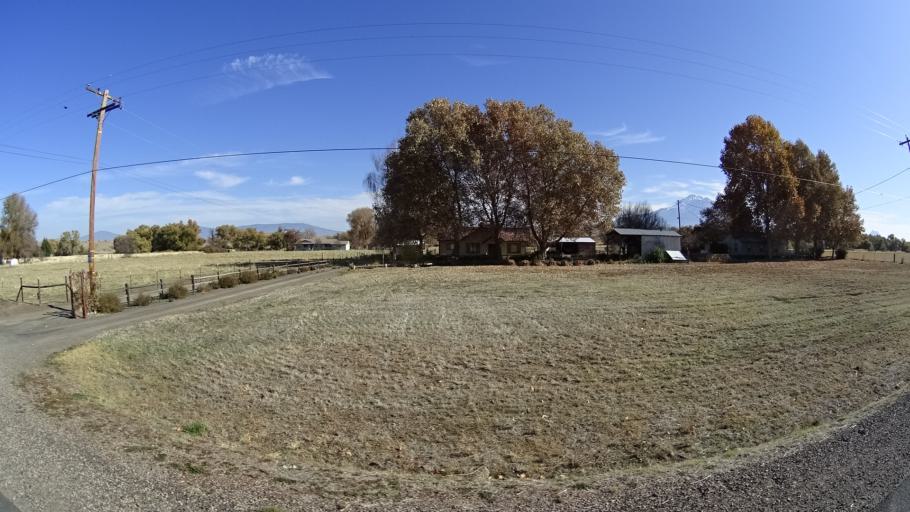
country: US
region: California
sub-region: Siskiyou County
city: Weed
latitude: 41.5154
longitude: -122.5187
